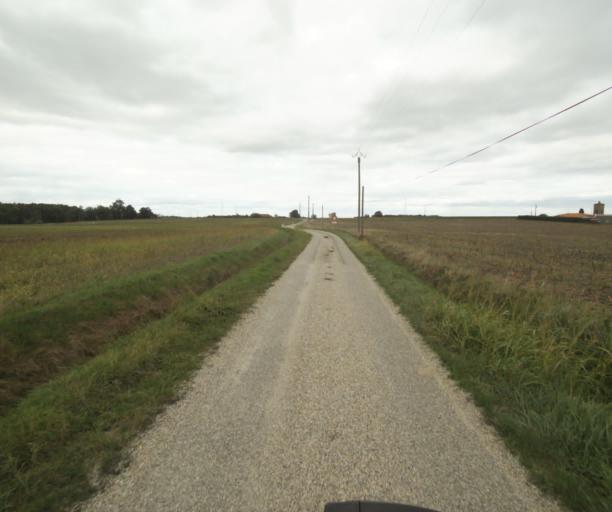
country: FR
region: Midi-Pyrenees
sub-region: Departement du Tarn-et-Garonne
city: Beaumont-de-Lomagne
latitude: 43.8625
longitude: 1.0692
